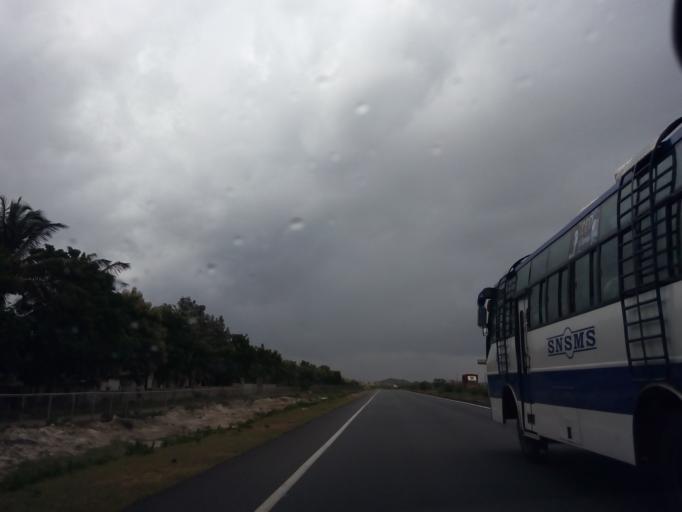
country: IN
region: Karnataka
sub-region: Chitradurga
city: Chitradurga
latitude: 14.2678
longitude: 76.3339
